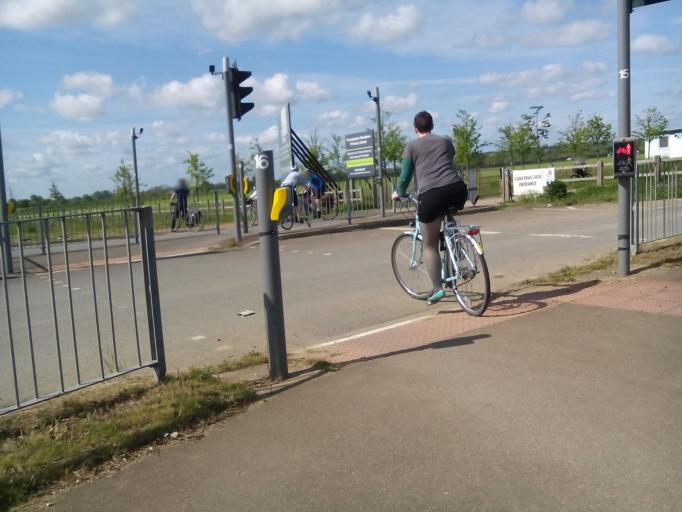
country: GB
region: England
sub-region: Cambridgeshire
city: Grantchester
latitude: 52.1648
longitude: 0.1067
